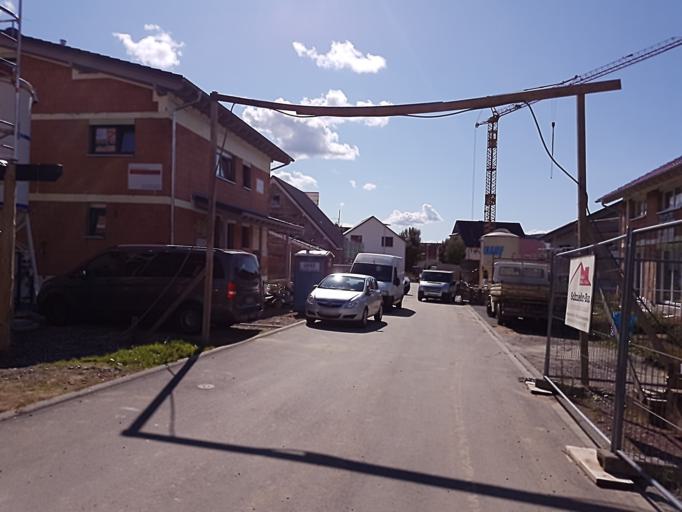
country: DE
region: Baden-Wuerttemberg
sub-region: Freiburg Region
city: Gutach im Breisgau
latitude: 48.1434
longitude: 8.0266
